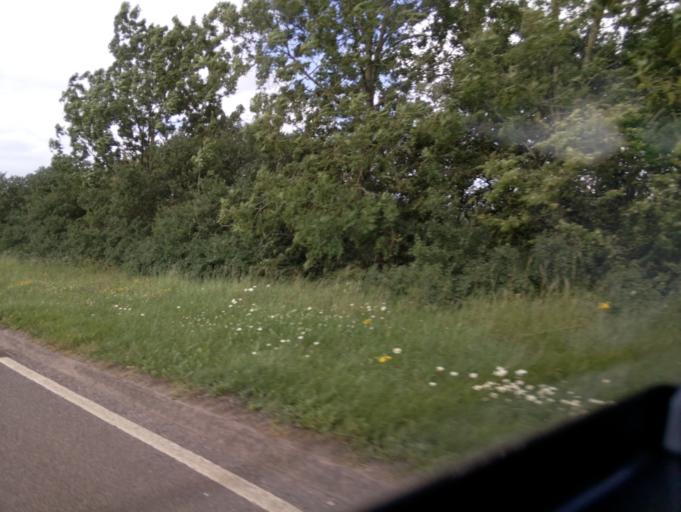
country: GB
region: England
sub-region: Leicestershire
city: Donisthorpe
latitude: 52.6853
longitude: -1.5461
